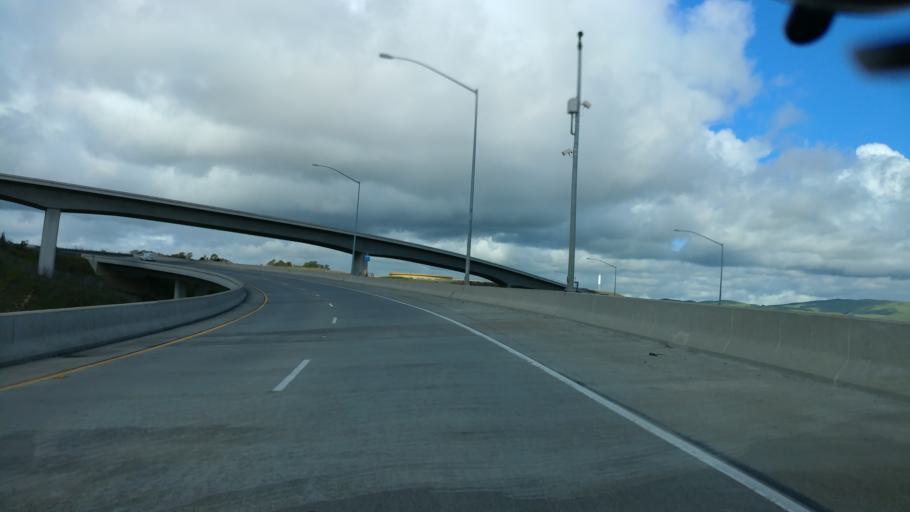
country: US
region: California
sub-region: Solano County
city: Benicia
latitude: 38.0503
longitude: -122.1277
